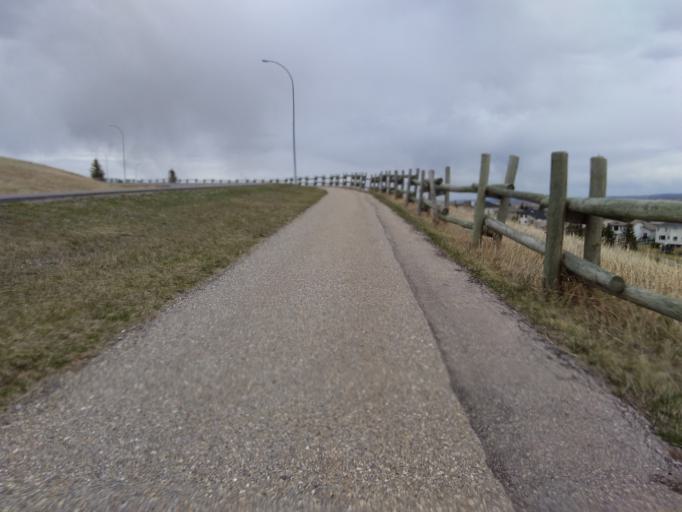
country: CA
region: Alberta
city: Cochrane
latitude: 51.1883
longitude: -114.4294
